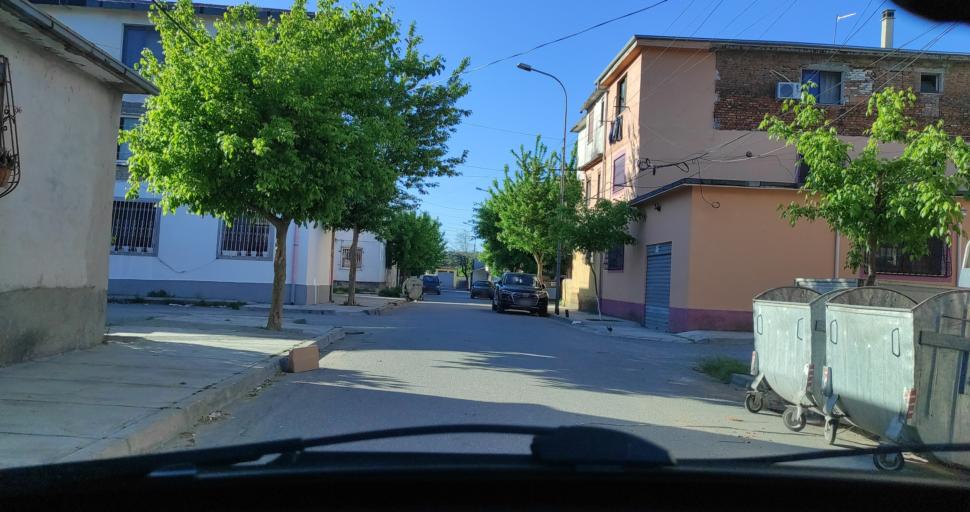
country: AL
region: Shkoder
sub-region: Rrethi i Shkodres
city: Shkoder
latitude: 42.0584
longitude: 19.5110
